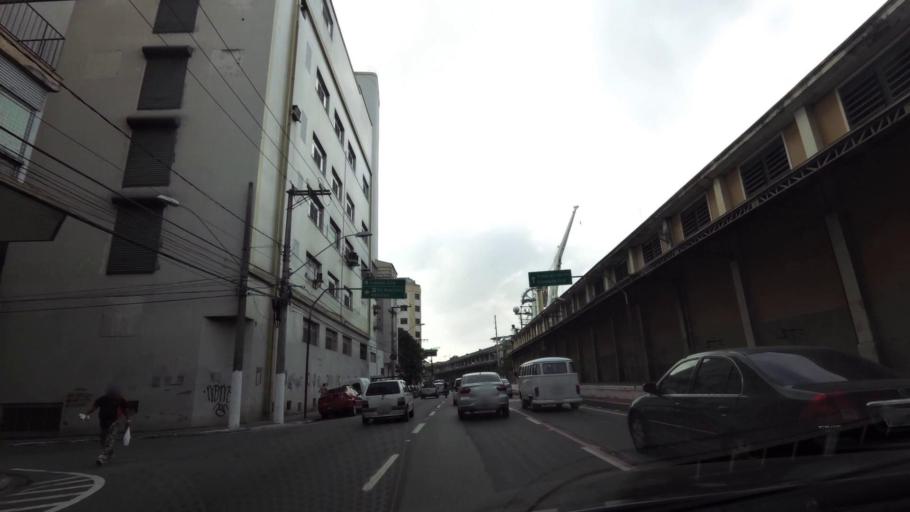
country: BR
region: Espirito Santo
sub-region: Vitoria
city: Vitoria
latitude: -20.3219
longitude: -40.3424
